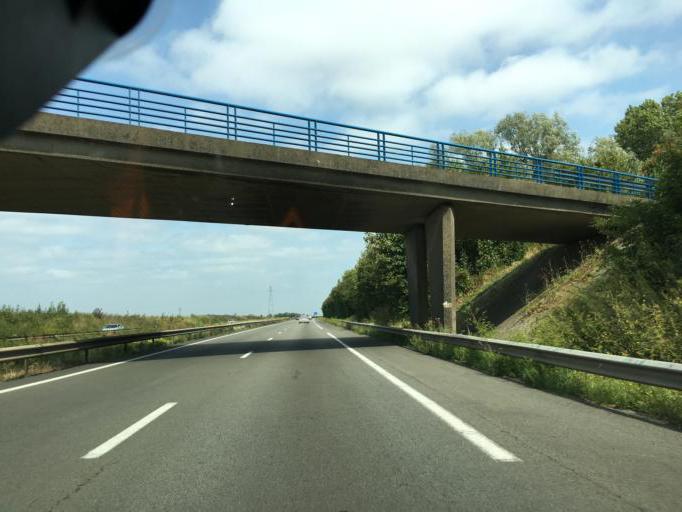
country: FR
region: Nord-Pas-de-Calais
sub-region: Departement du Nord
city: Saultain
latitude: 50.3587
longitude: 3.5863
